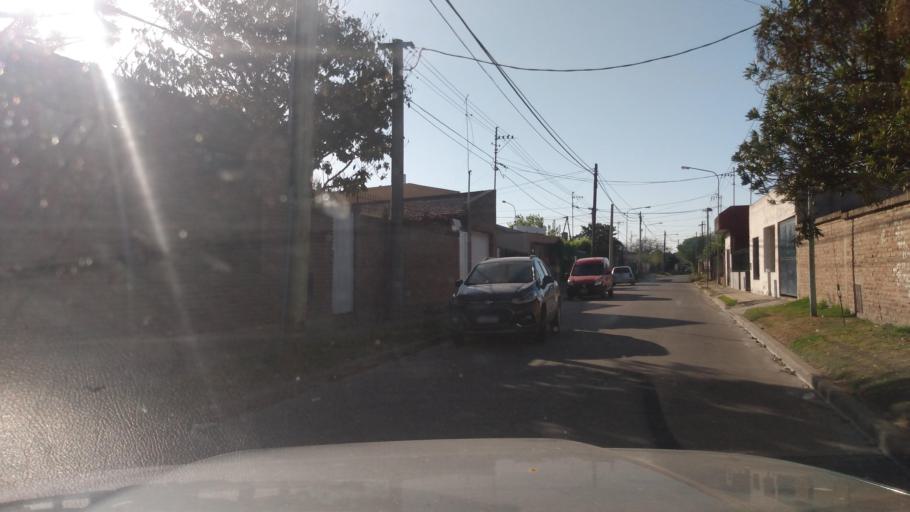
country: AR
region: Buenos Aires
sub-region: Partido de Lujan
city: Lujan
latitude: -34.5555
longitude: -59.1144
